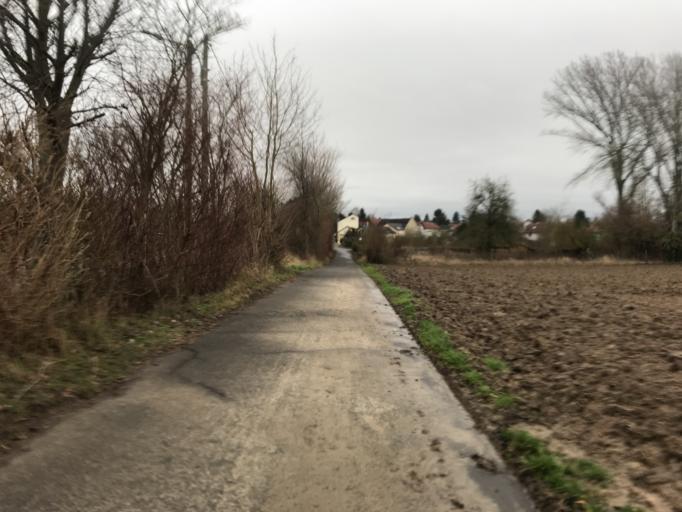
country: DE
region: Rheinland-Pfalz
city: Hahnheim
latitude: 49.8643
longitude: 8.2349
